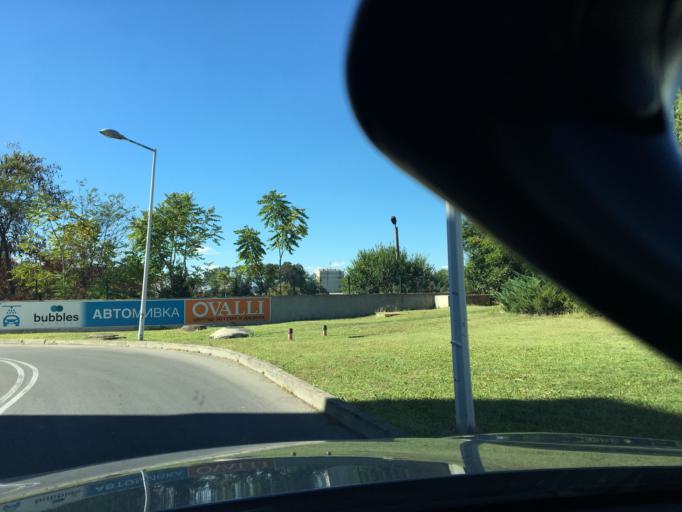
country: BG
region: Burgas
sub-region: Obshtina Burgas
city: Burgas
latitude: 42.5129
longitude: 27.4529
